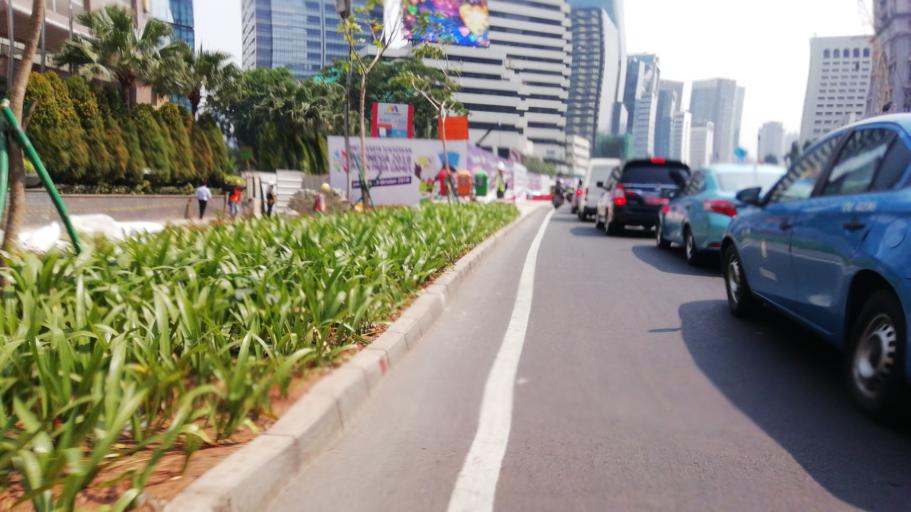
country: ID
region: Jakarta Raya
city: Jakarta
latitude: -6.2082
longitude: 106.8220
